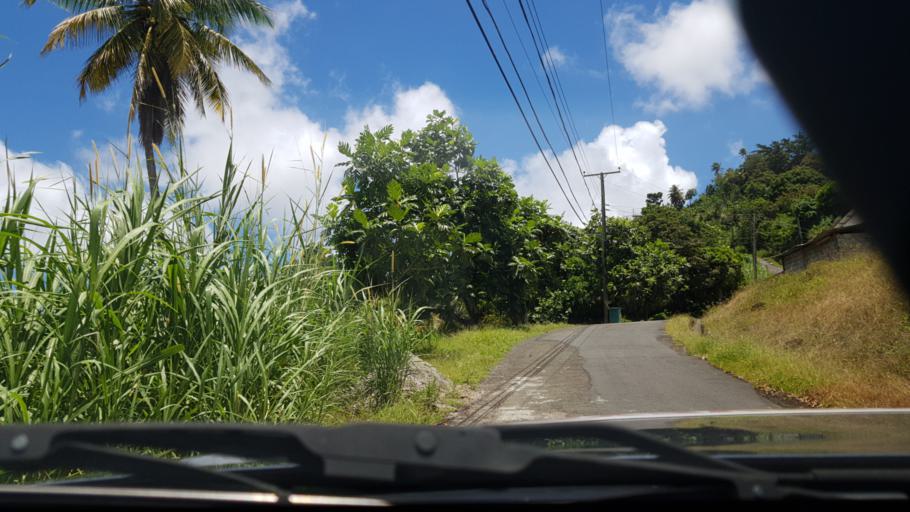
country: LC
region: Castries Quarter
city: Castries
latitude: 13.9567
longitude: -61.0002
